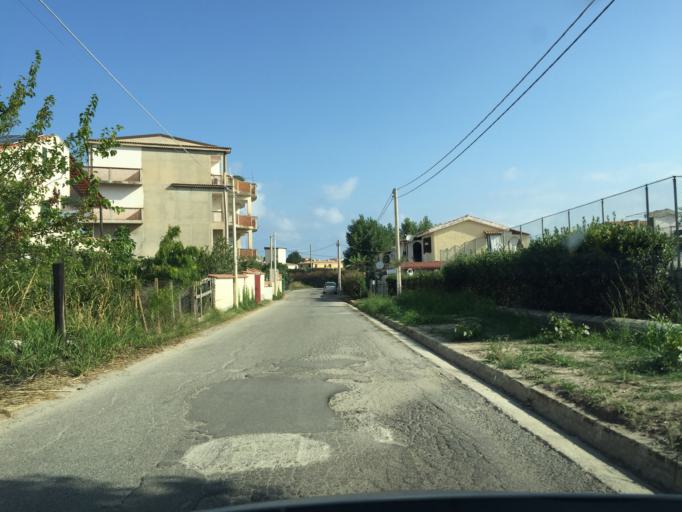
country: IT
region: Calabria
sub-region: Provincia di Vibo-Valentia
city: Briatico
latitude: 38.7196
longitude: 16.0548
